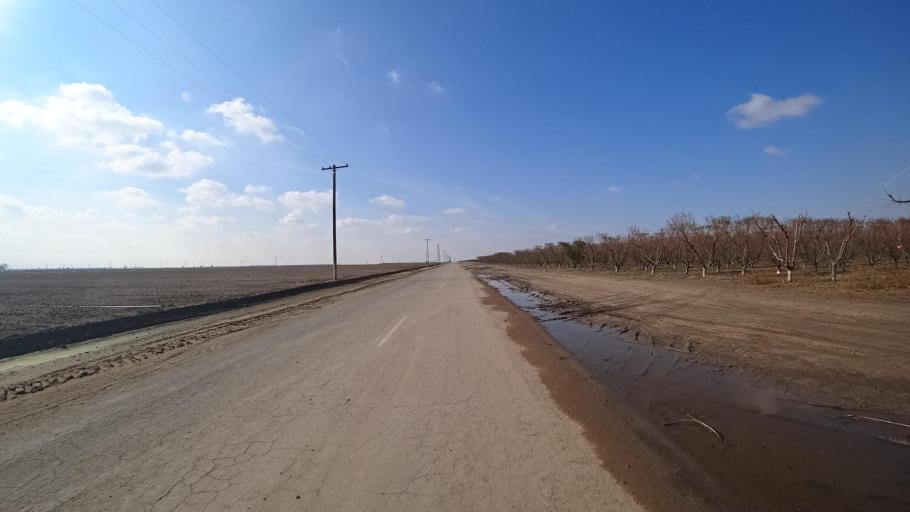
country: US
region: California
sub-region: Kern County
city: Arvin
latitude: 35.2530
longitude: -118.7995
